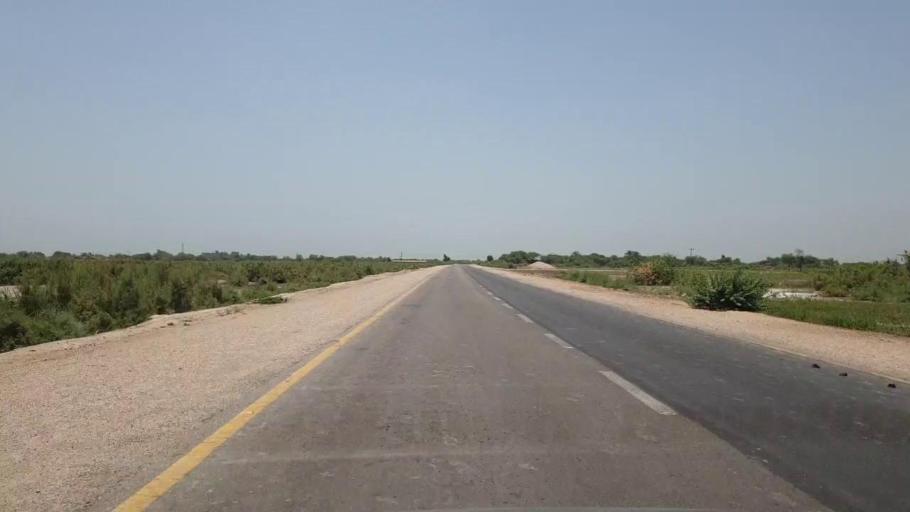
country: PK
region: Sindh
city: Sakrand
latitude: 26.1261
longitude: 68.3803
